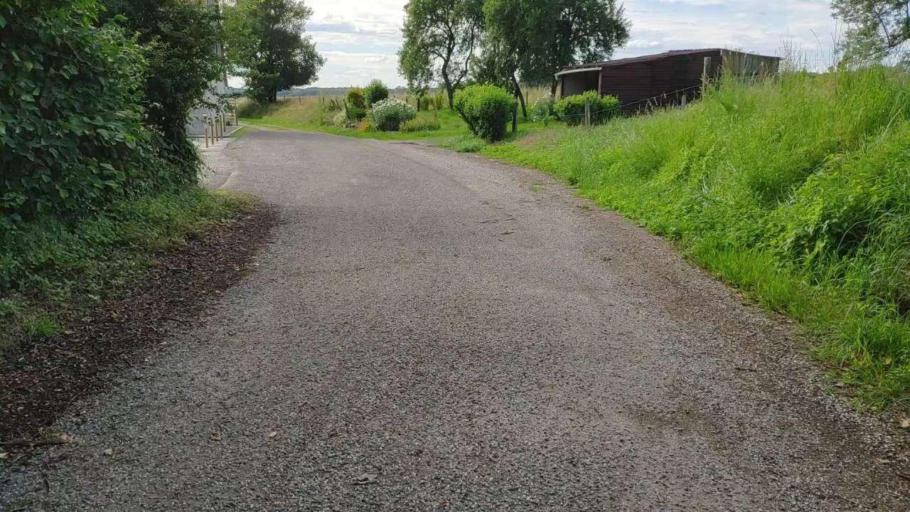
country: FR
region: Franche-Comte
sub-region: Departement du Jura
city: Bletterans
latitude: 46.8461
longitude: 5.5056
